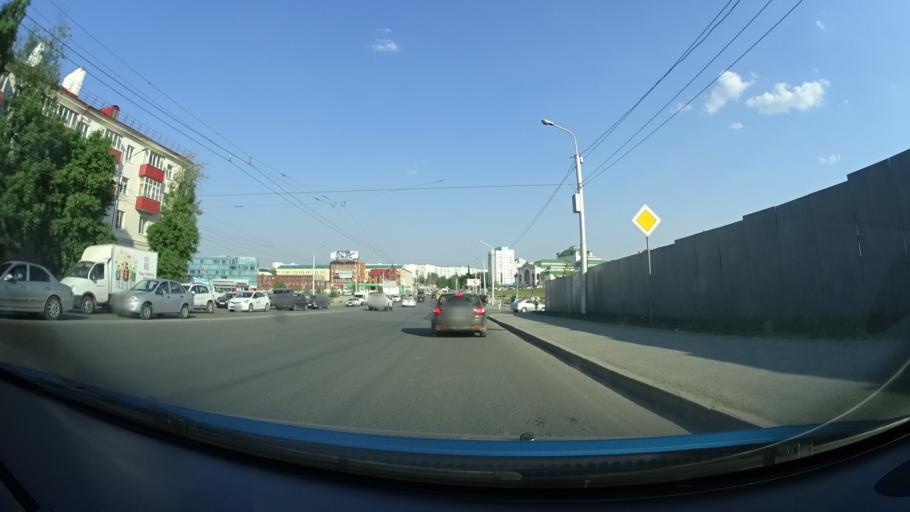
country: RU
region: Bashkortostan
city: Ufa
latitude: 54.7513
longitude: 56.0153
